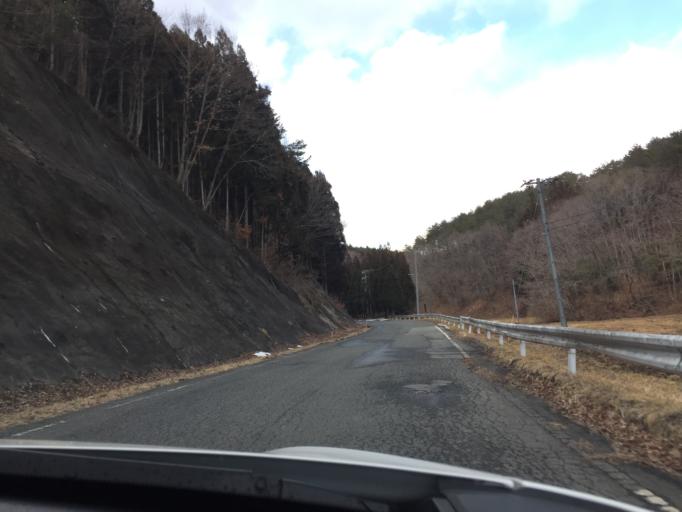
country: JP
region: Fukushima
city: Iwaki
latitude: 37.2247
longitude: 140.7419
